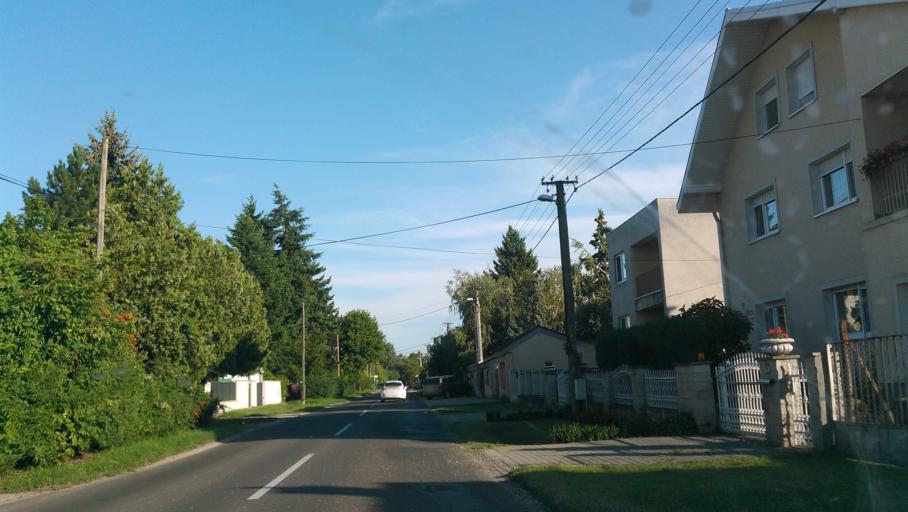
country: SK
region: Bratislavsky
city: Svaty Jur
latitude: 48.1872
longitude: 17.2618
